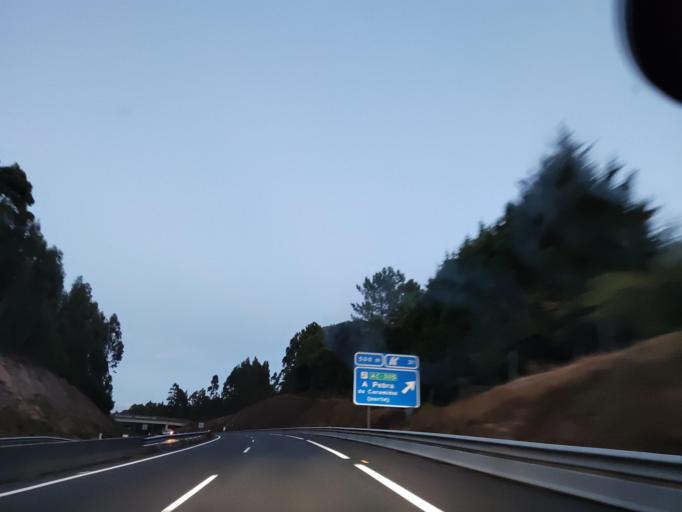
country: ES
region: Galicia
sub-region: Provincia da Coruna
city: Boiro
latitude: 42.6232
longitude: -8.9377
